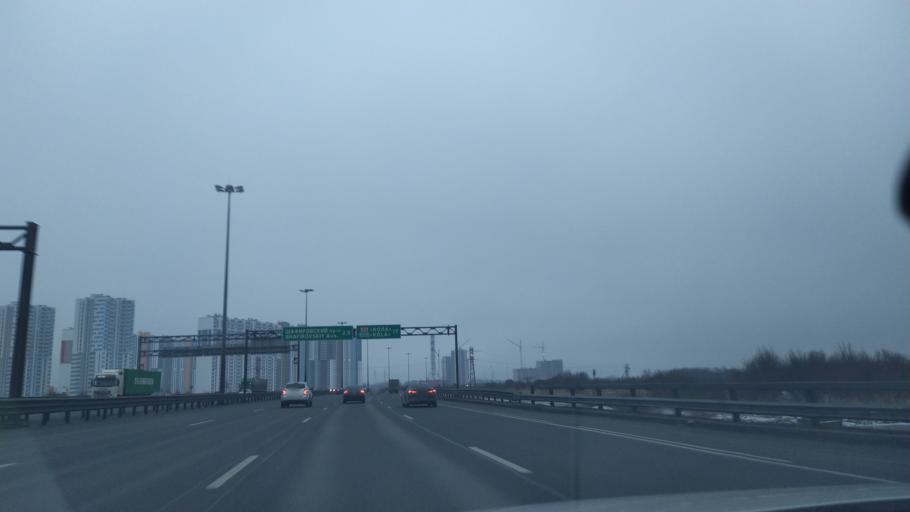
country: RU
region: Leningrad
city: Murino
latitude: 60.0139
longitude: 30.4697
